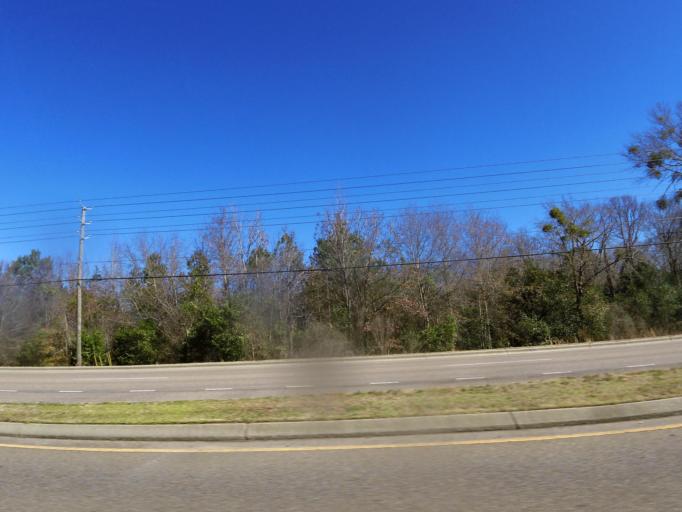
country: US
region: Alabama
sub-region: Elmore County
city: Millbrook
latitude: 32.4771
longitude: -86.4042
